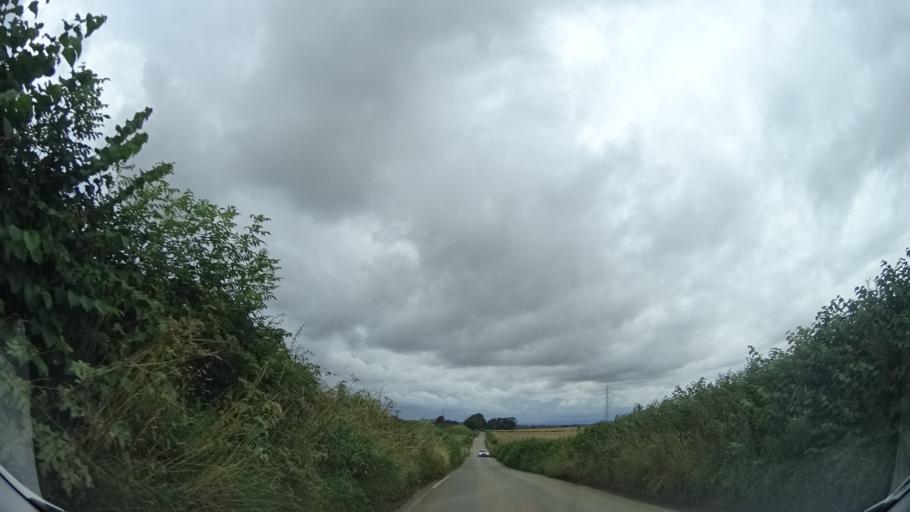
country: GB
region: Scotland
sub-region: West Lothian
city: Kirknewton
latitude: 55.9016
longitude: -3.4338
